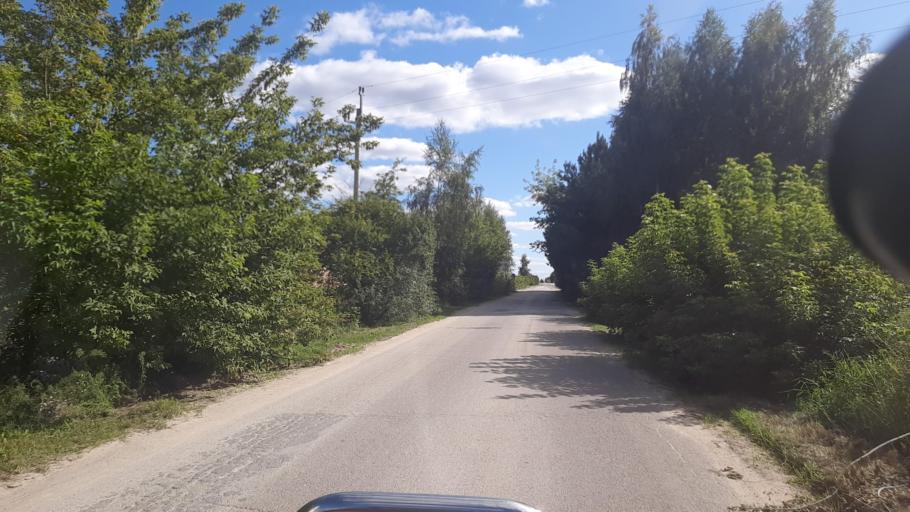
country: PL
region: Lublin Voivodeship
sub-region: Powiat pulawski
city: Markuszow
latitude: 51.4146
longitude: 22.2292
